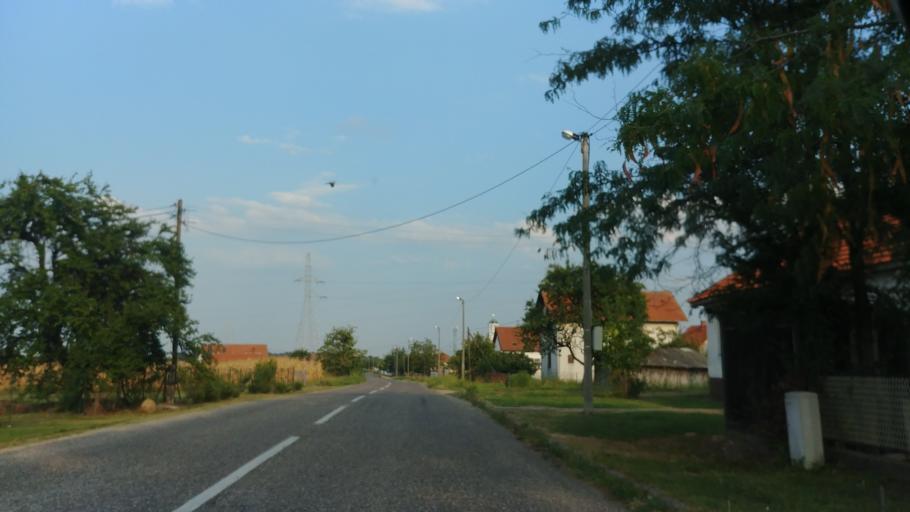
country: BA
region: Republika Srpska
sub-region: Opstina Ugljevik
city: Ugljevik
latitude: 44.7071
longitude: 18.9899
